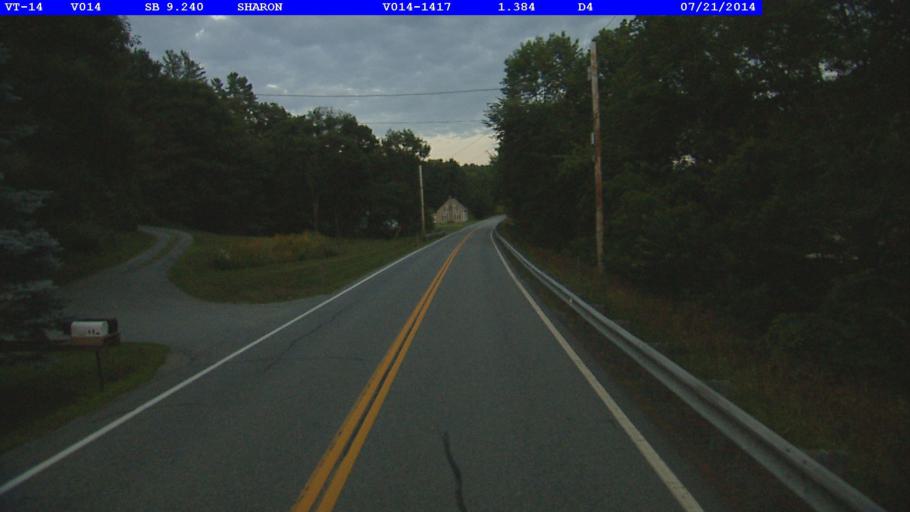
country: US
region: Vermont
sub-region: Windsor County
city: Woodstock
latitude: 43.7388
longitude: -72.4378
